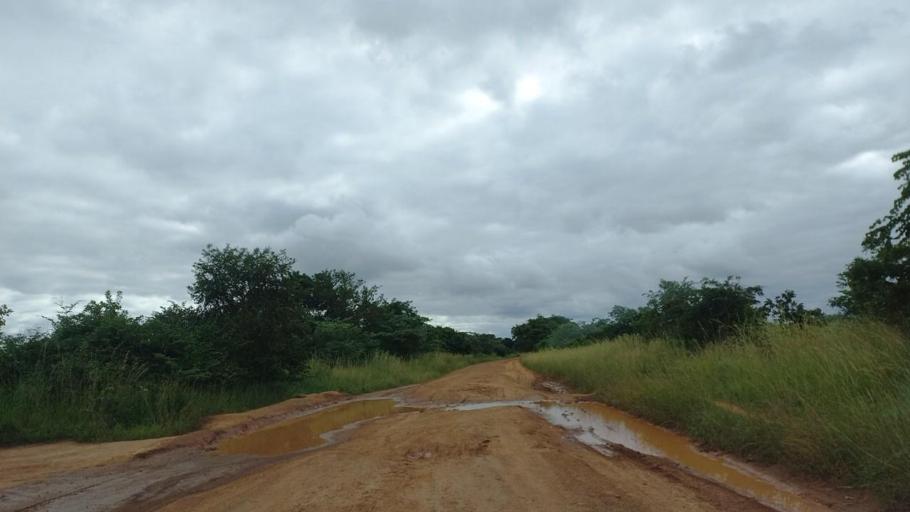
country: ZM
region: Lusaka
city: Chongwe
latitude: -15.4564
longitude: 28.8671
